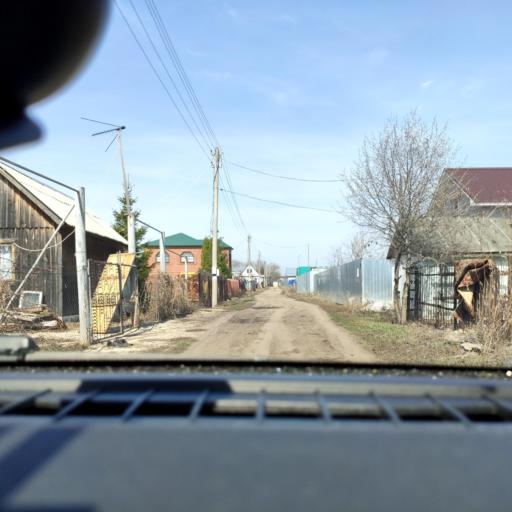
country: RU
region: Samara
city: Podstepki
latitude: 53.5180
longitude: 49.1080
